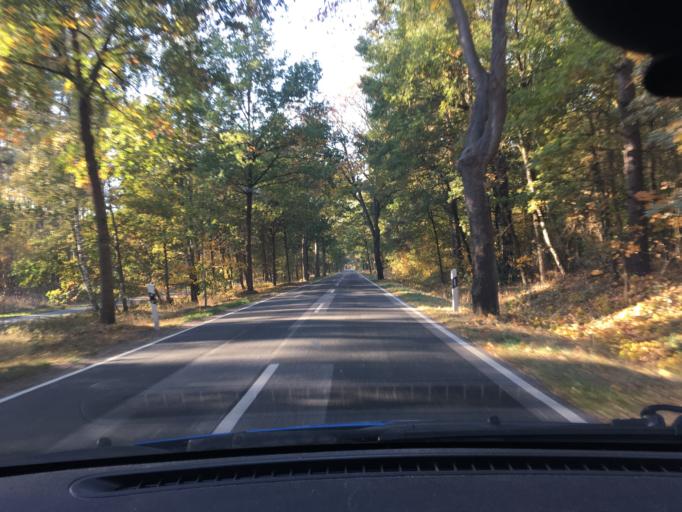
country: DE
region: Lower Saxony
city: Damnatz
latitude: 53.1569
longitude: 11.2063
